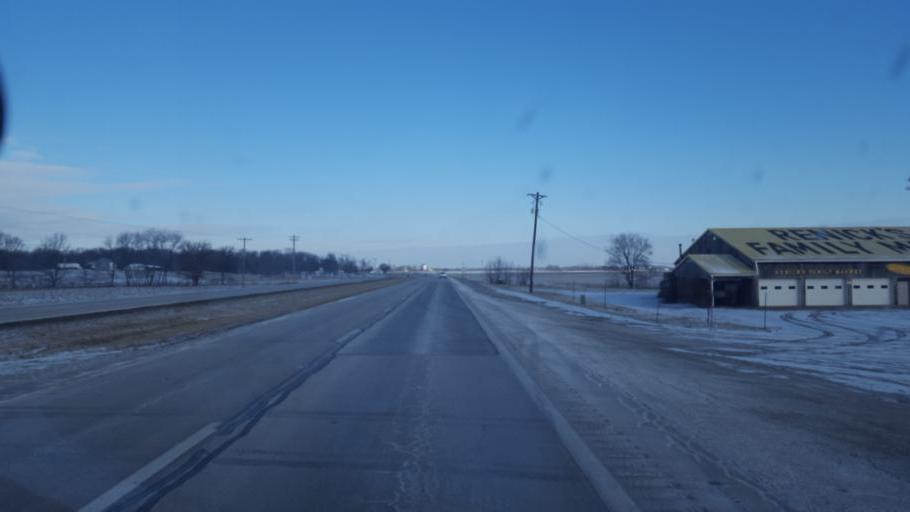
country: US
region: Ohio
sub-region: Pickaway County
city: South Bloomfield
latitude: 39.7299
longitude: -82.9864
